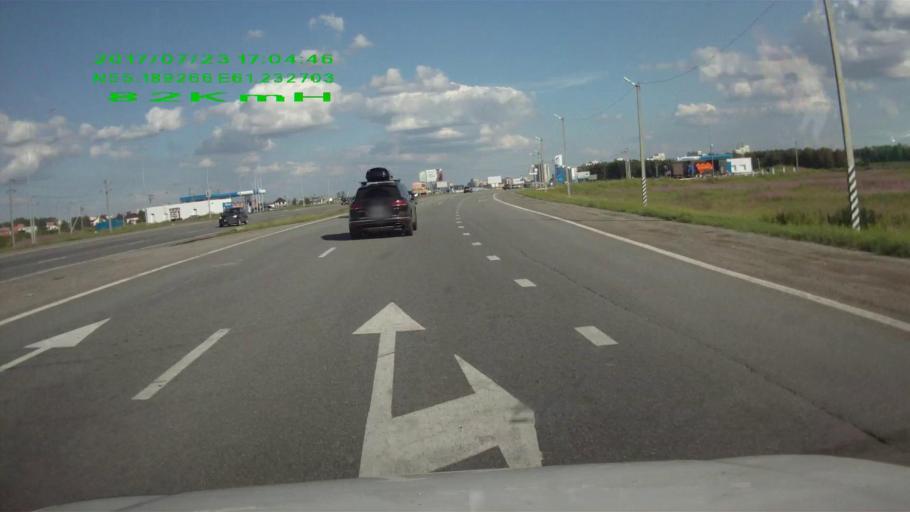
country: RU
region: Chelyabinsk
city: Roshchino
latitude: 55.1888
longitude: 61.2341
